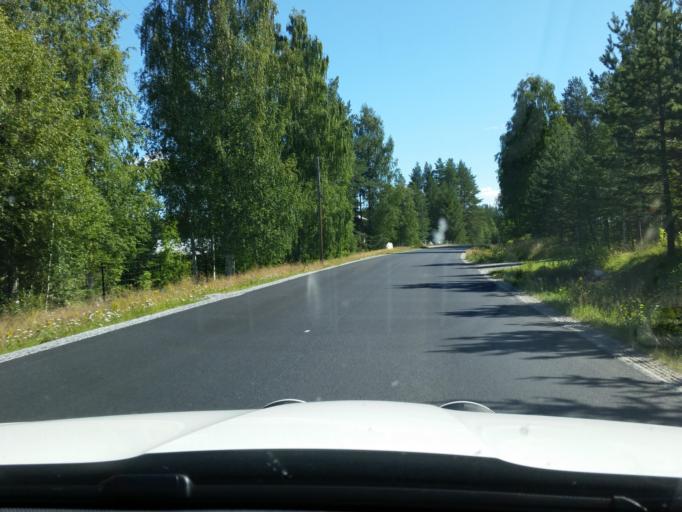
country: SE
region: Norrbotten
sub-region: Pitea Kommun
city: Roknas
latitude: 65.3471
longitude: 21.1188
